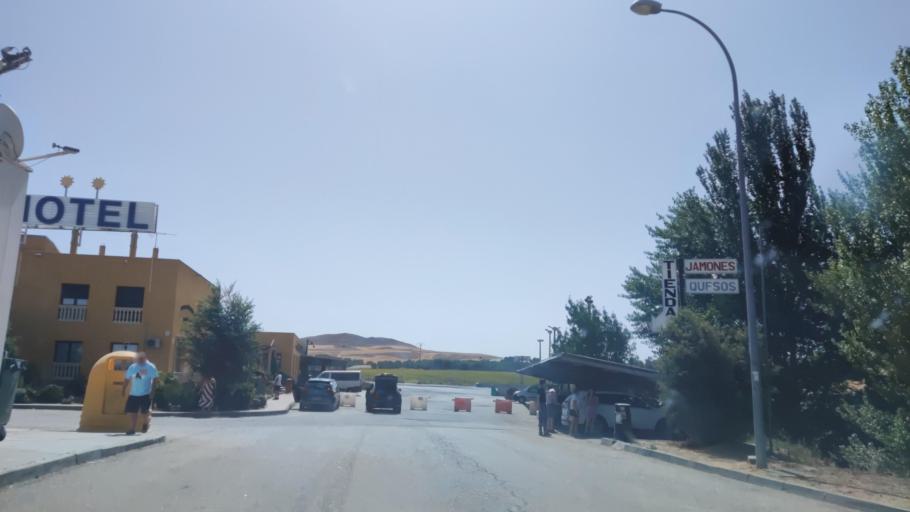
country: ES
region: Castille-La Mancha
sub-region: Provincia de Cuenca
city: Montalbo
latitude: 39.9037
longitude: -2.7143
